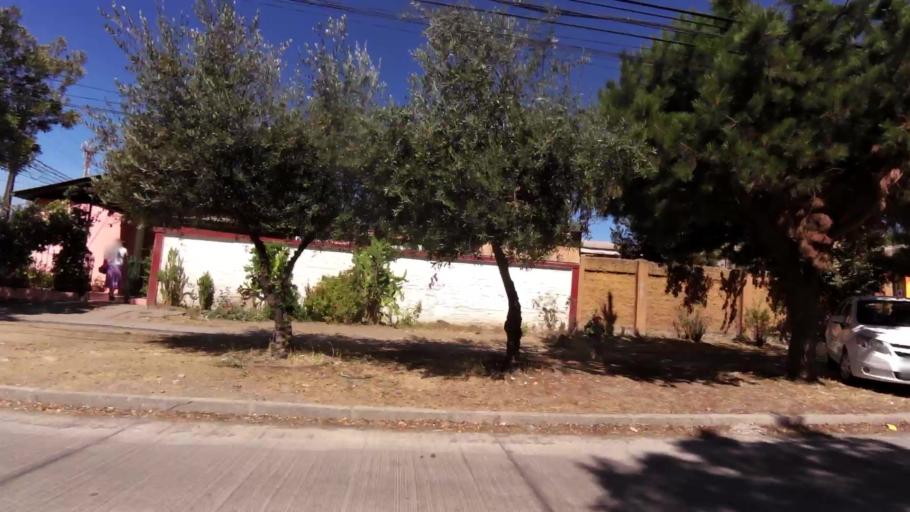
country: CL
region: O'Higgins
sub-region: Provincia de Colchagua
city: Chimbarongo
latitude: -34.5732
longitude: -70.9944
